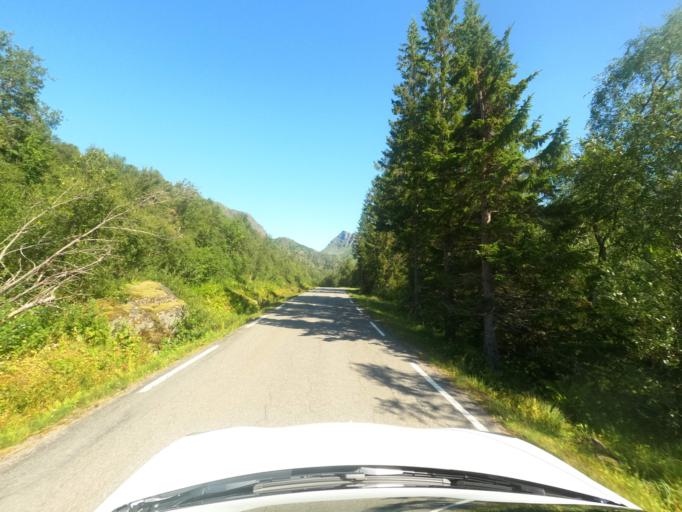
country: NO
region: Nordland
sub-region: Hadsel
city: Stokmarknes
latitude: 68.3056
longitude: 15.0518
